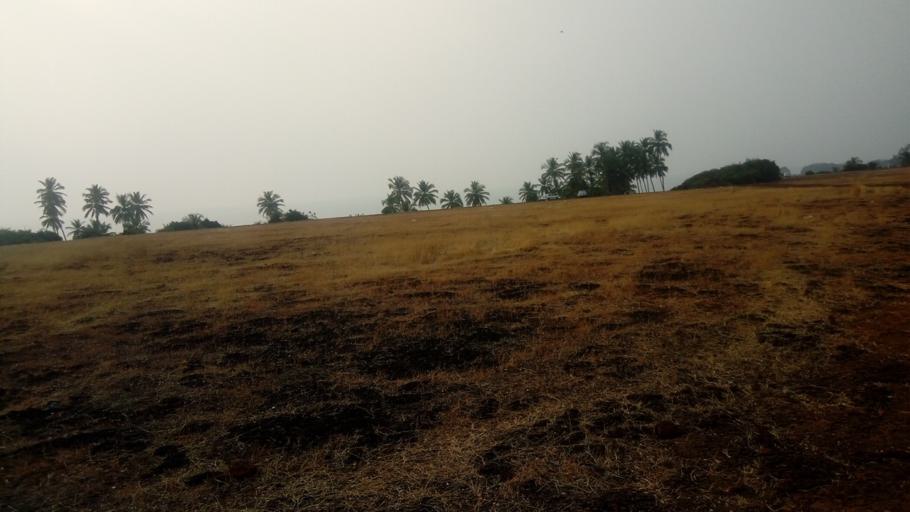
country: IN
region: Goa
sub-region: South Goa
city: Cavelossim
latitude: 15.1002
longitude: 73.9282
